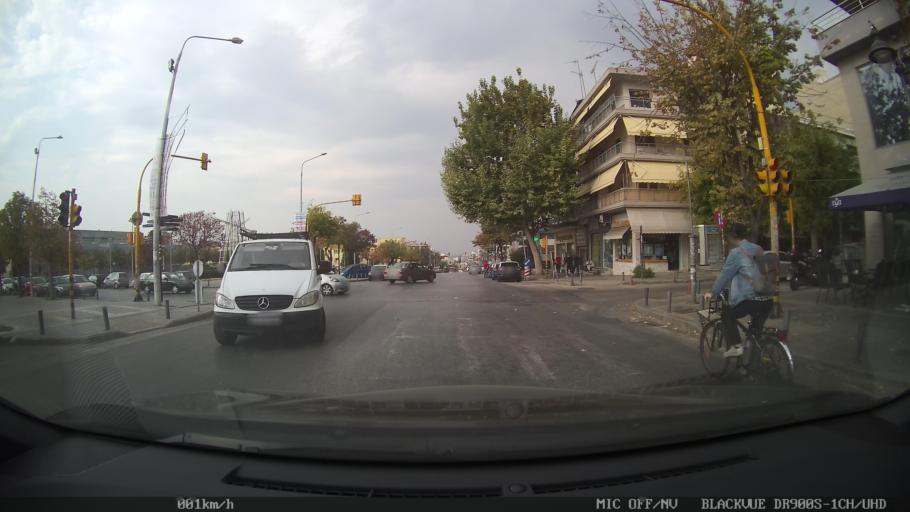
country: GR
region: Central Macedonia
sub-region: Nomos Thessalonikis
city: Triandria
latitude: 40.6161
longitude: 22.9736
